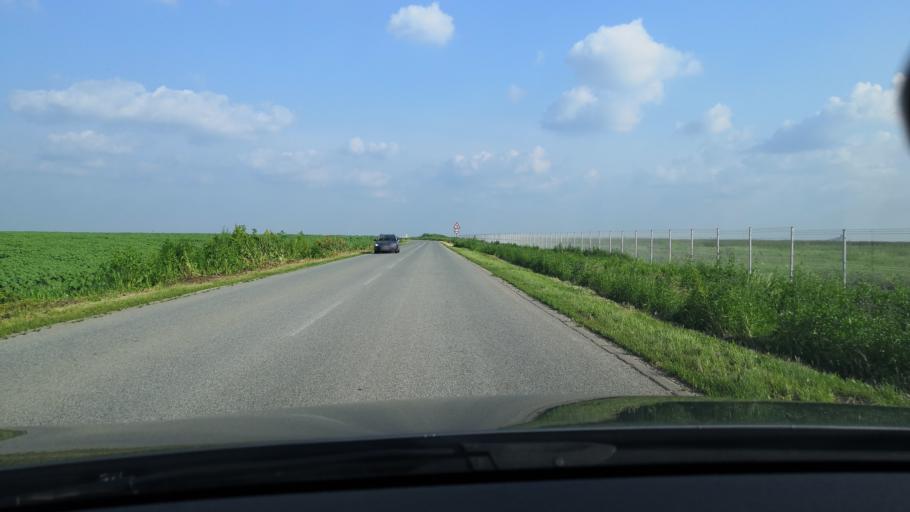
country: RS
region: Autonomna Pokrajina Vojvodina
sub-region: Sremski Okrug
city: Ingija
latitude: 45.0926
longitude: 20.0964
